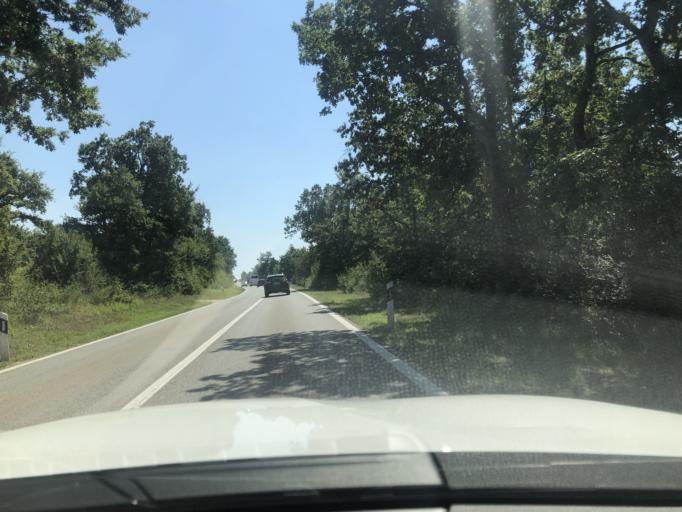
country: HR
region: Istarska
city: Vodnjan
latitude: 45.0182
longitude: 13.8041
